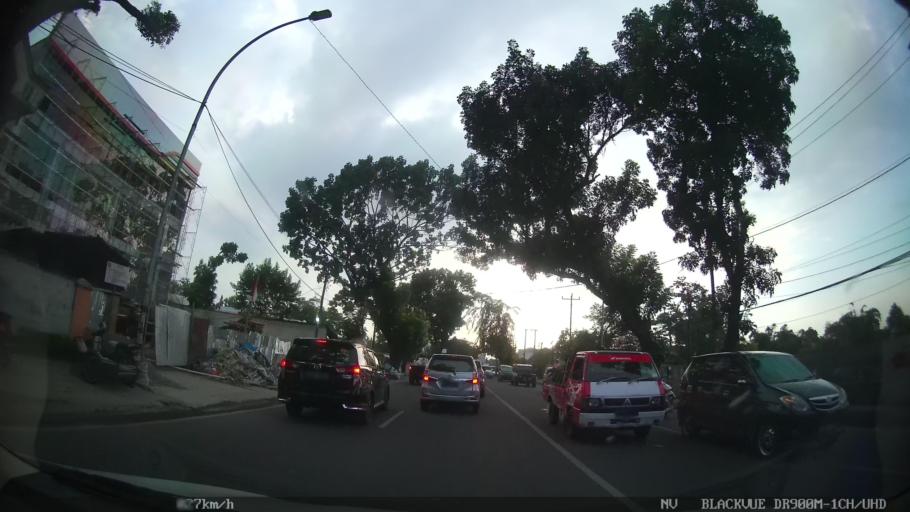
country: ID
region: North Sumatra
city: Medan
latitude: 3.6062
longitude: 98.6725
